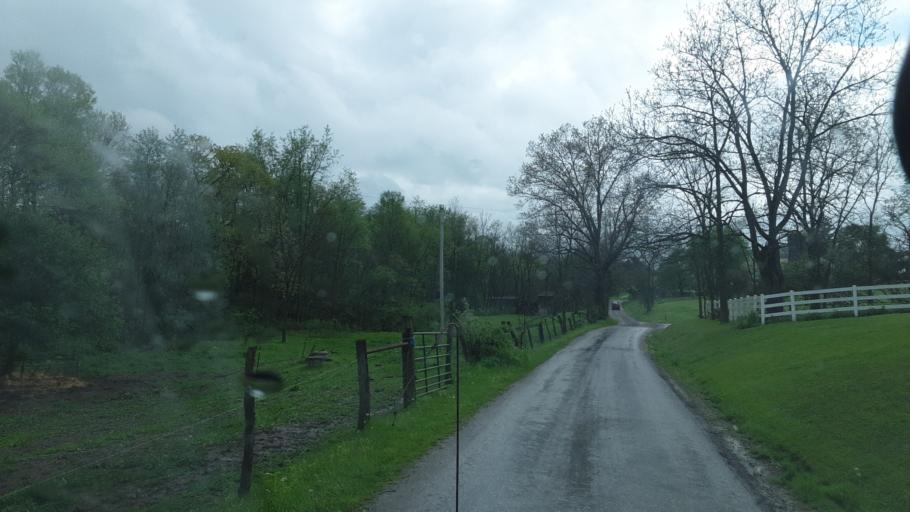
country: US
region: Ohio
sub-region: Holmes County
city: Millersburg
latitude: 40.5008
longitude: -81.8309
